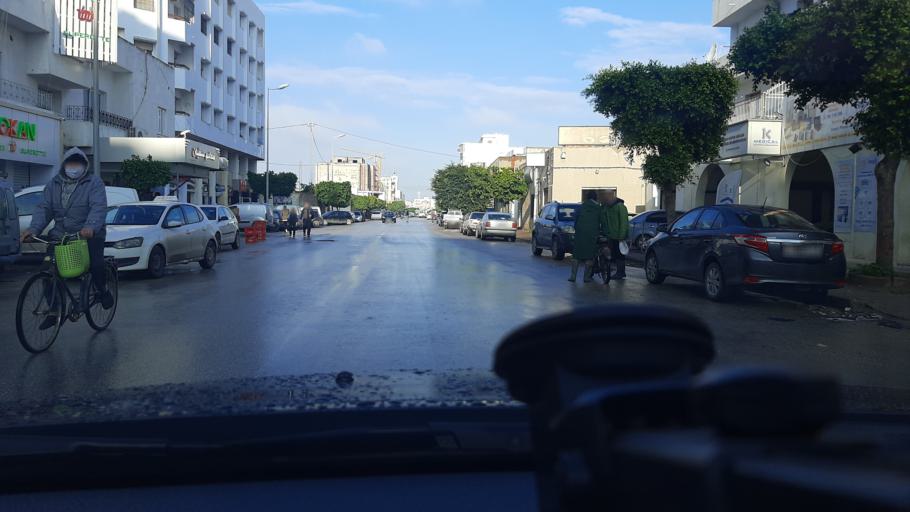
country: TN
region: Safaqis
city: Sfax
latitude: 34.7431
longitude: 10.7539
